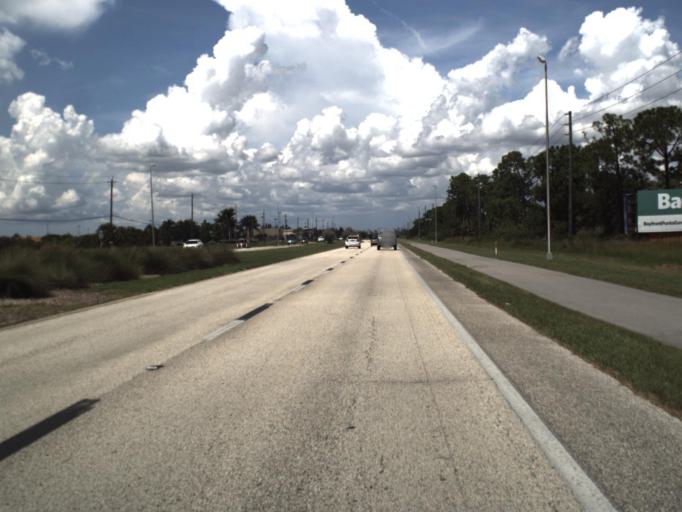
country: US
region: Florida
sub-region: Charlotte County
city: Charlotte Park
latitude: 26.8931
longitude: -82.0252
